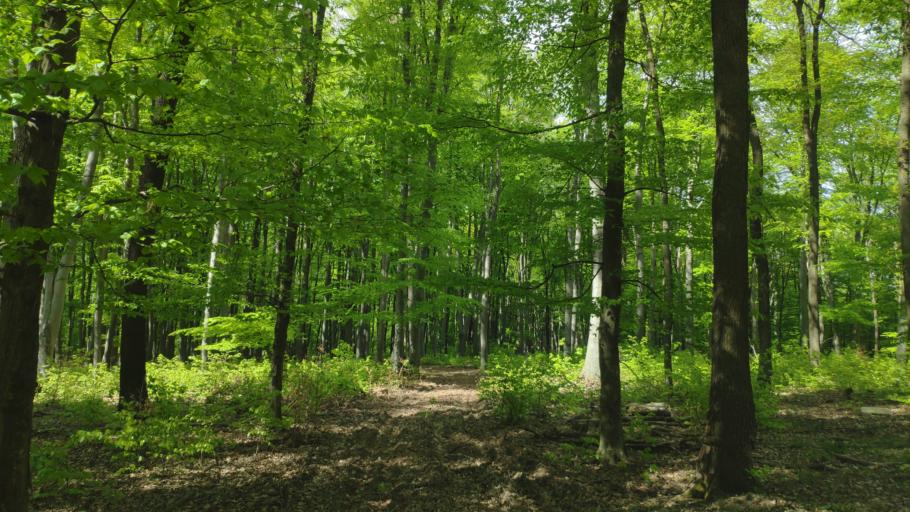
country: SK
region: Kosicky
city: Kosice
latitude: 48.6674
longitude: 21.4481
